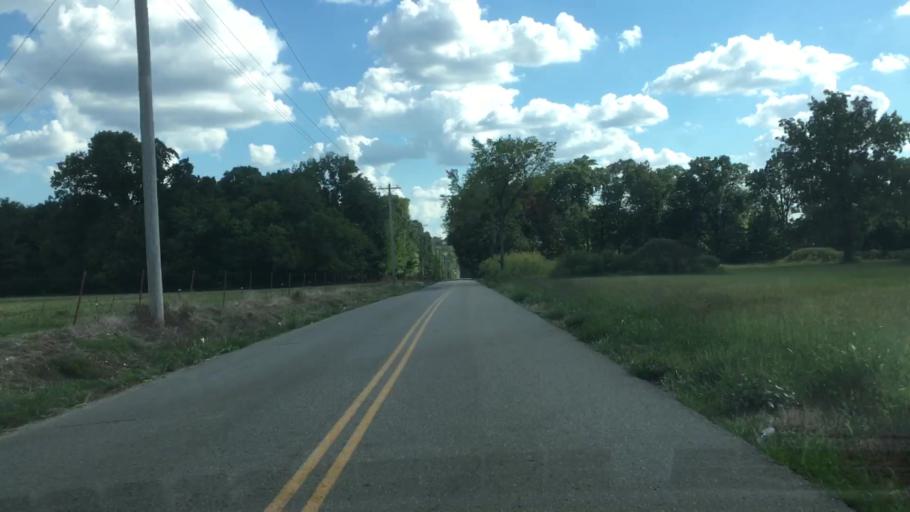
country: US
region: Oklahoma
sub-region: Cherokee County
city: Park Hill
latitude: 35.8051
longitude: -95.0739
